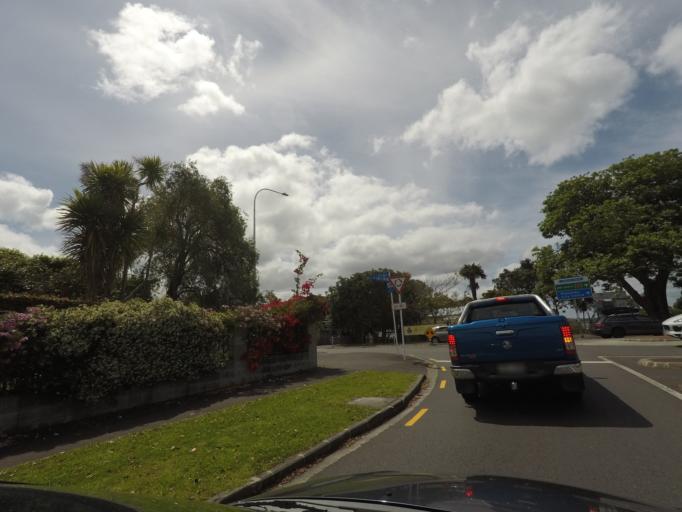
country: NZ
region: Auckland
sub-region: Auckland
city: Auckland
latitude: -36.8485
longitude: 174.7301
